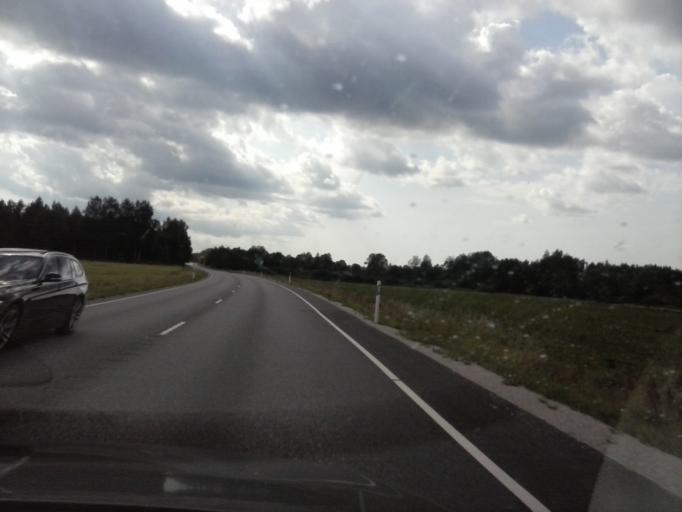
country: EE
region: Jaervamaa
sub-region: Tueri vald
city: Sarevere
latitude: 58.7545
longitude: 25.3367
